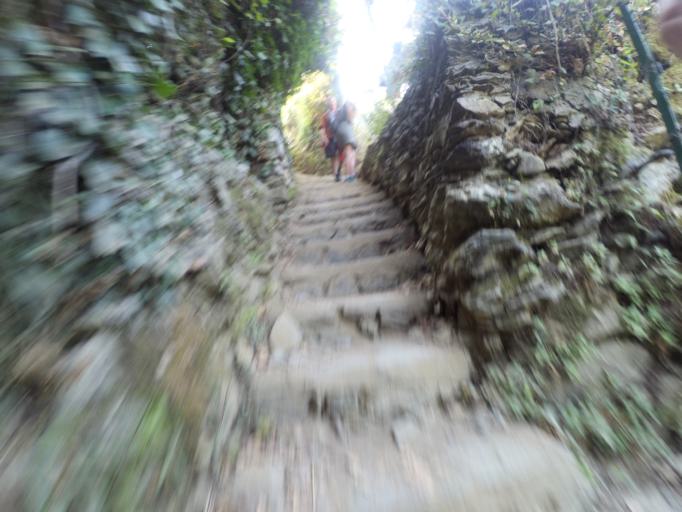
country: IT
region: Liguria
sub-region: Provincia di La Spezia
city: Monterosso al Mare
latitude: 44.1450
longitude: 9.6620
